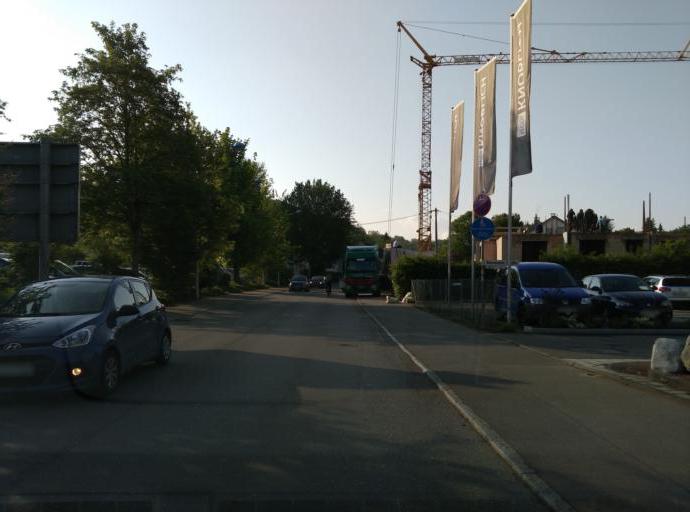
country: DE
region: Baden-Wuerttemberg
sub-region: Tuebingen Region
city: Kirchentellinsfurt
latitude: 48.5307
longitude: 9.1394
